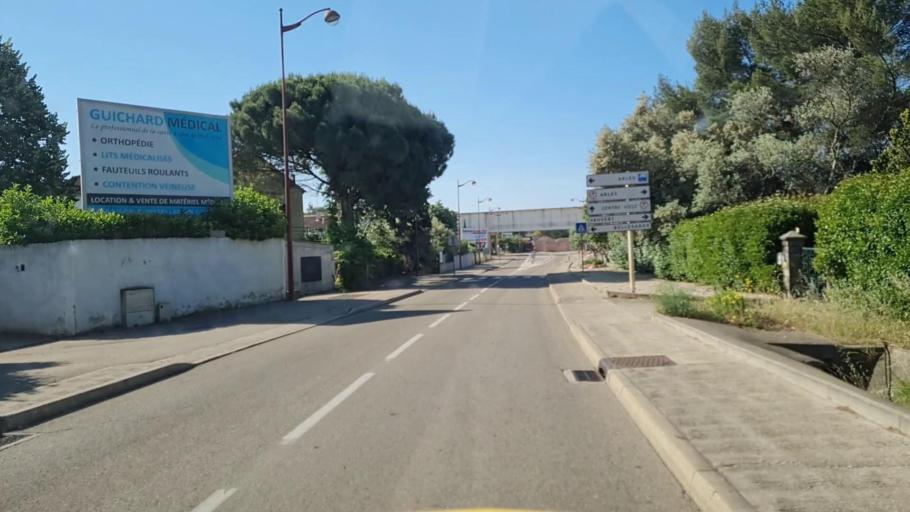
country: FR
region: Languedoc-Roussillon
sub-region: Departement du Gard
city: Saint-Gilles
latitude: 43.6845
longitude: 4.4296
